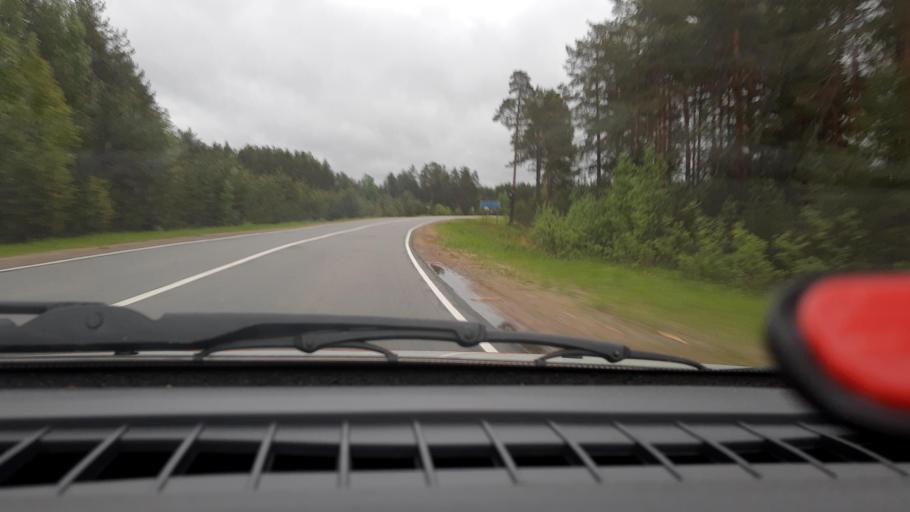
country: RU
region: Nizjnij Novgorod
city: Krasnyye Baki
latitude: 57.2140
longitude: 45.4661
